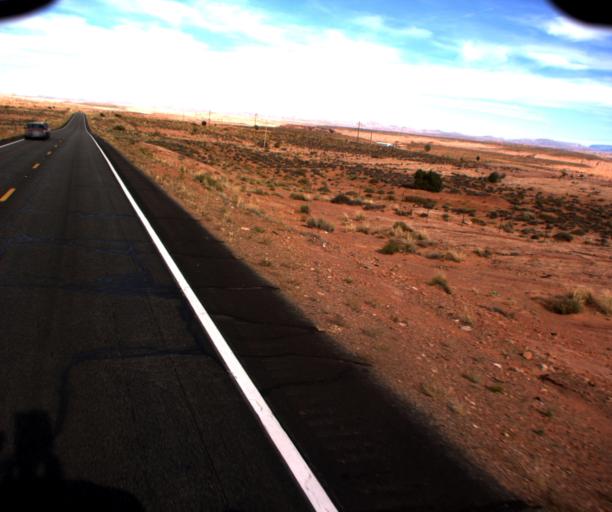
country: US
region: Arizona
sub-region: Navajo County
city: Kayenta
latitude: 36.9296
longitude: -109.7504
